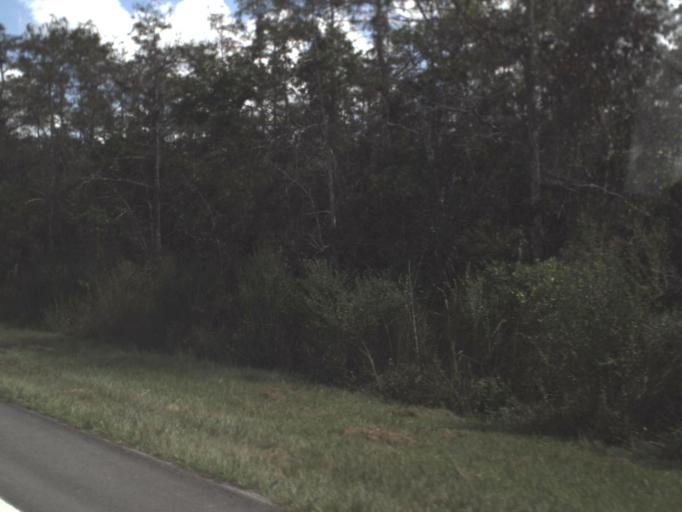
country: US
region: Florida
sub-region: Miami-Dade County
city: Kendall West
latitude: 25.8514
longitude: -80.9789
